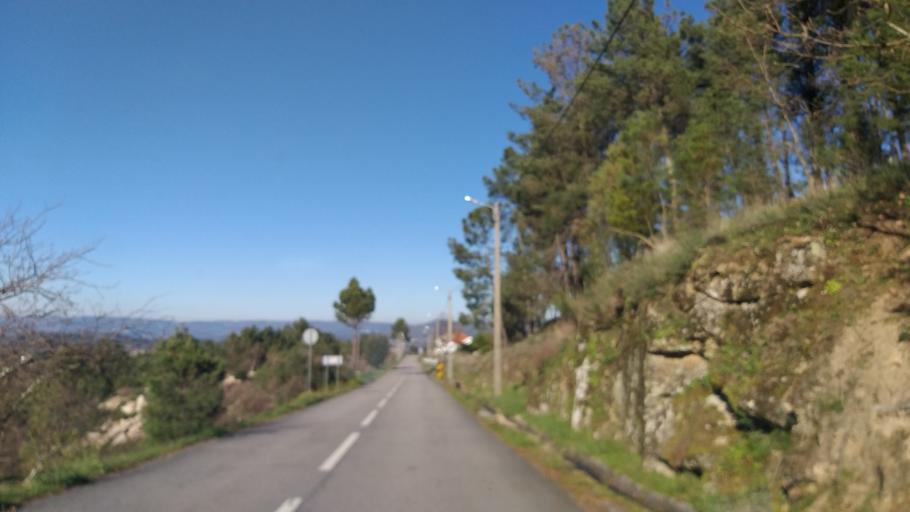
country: PT
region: Guarda
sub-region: Celorico da Beira
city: Celorico da Beira
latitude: 40.5877
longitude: -7.3601
